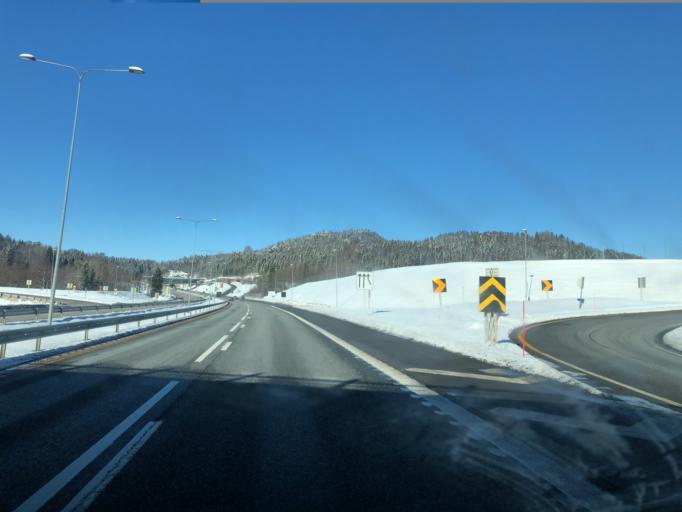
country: NO
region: Vestfold
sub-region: Holmestrand
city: Gullhaug
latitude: 59.5090
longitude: 10.2110
